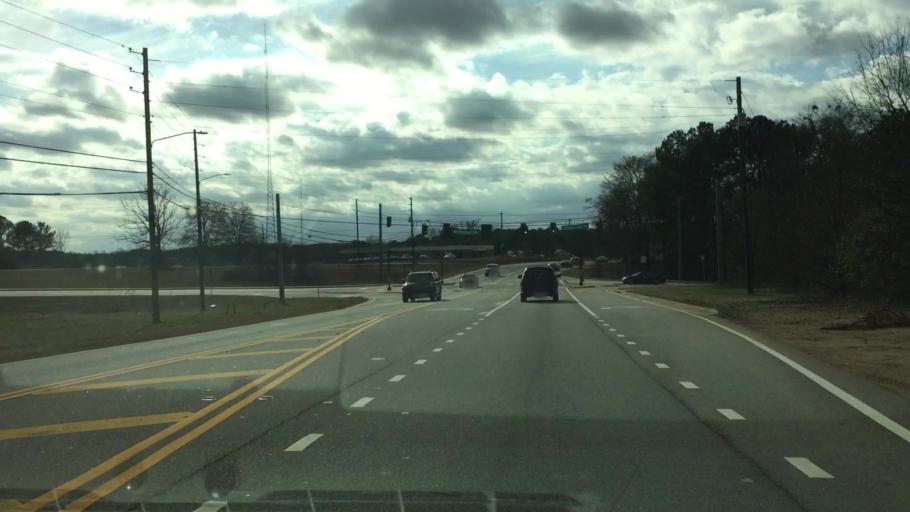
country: US
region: Georgia
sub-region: Henry County
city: McDonough
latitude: 33.4366
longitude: -84.1598
